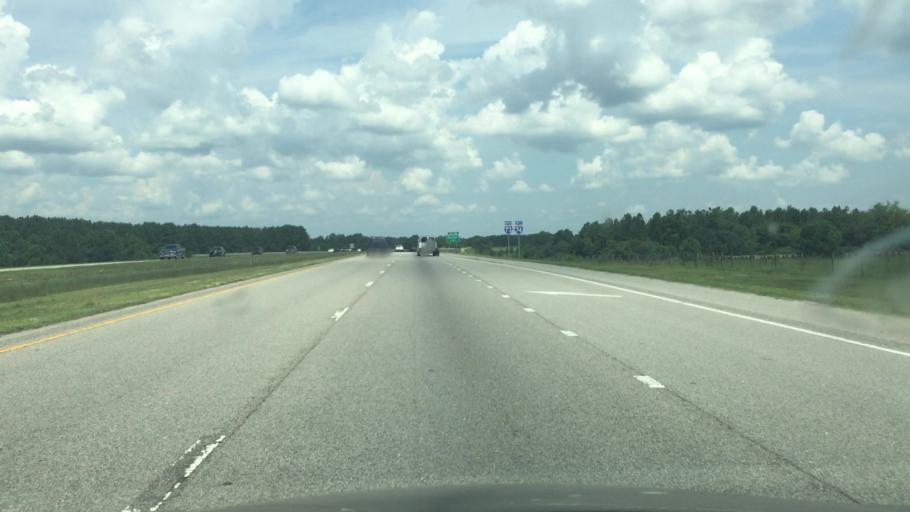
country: US
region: North Carolina
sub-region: Richmond County
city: Ellerbe
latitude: 35.1524
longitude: -79.7149
